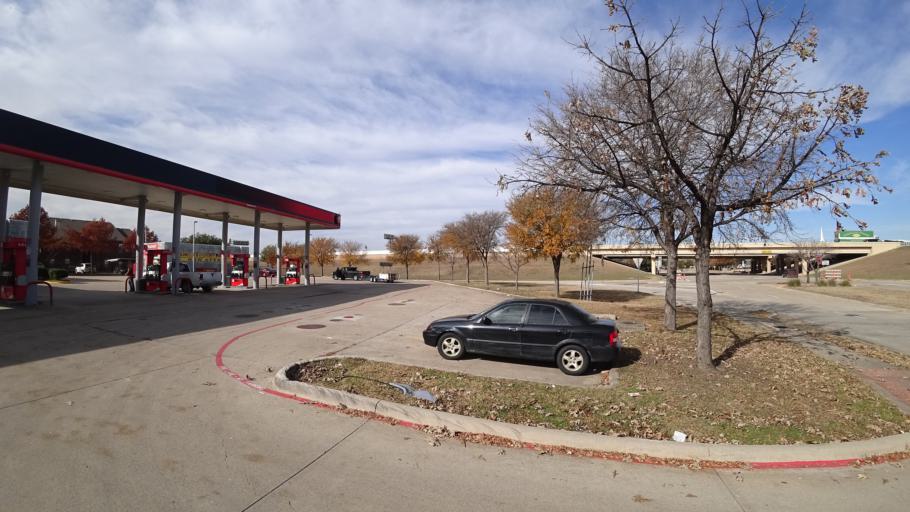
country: US
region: Texas
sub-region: Denton County
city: Lewisville
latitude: 33.0111
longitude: -96.9425
